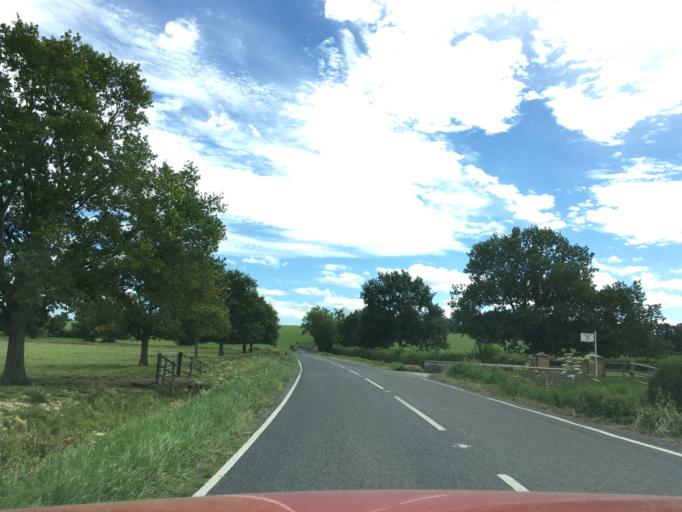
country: GB
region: England
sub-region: Somerset
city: Glastonbury
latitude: 51.1215
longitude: -2.7114
